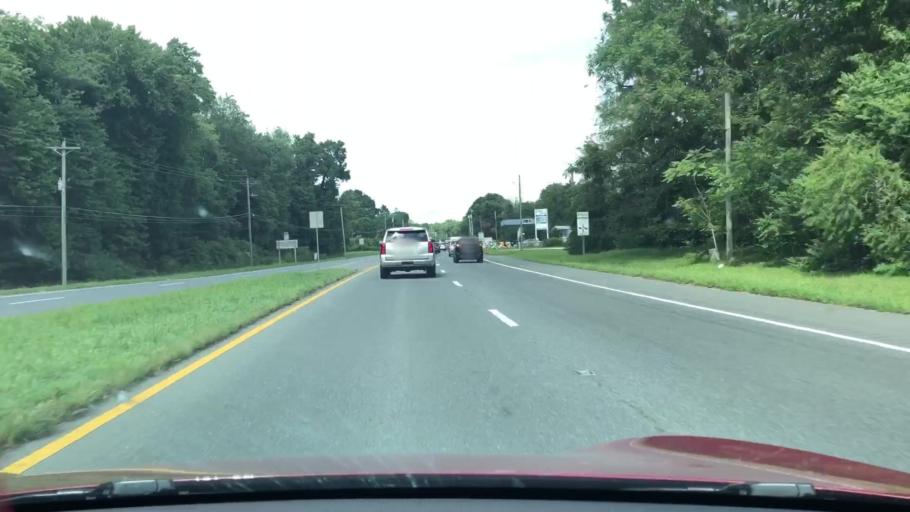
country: US
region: Virginia
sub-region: Accomack County
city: Wattsville
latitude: 37.9316
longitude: -75.5479
